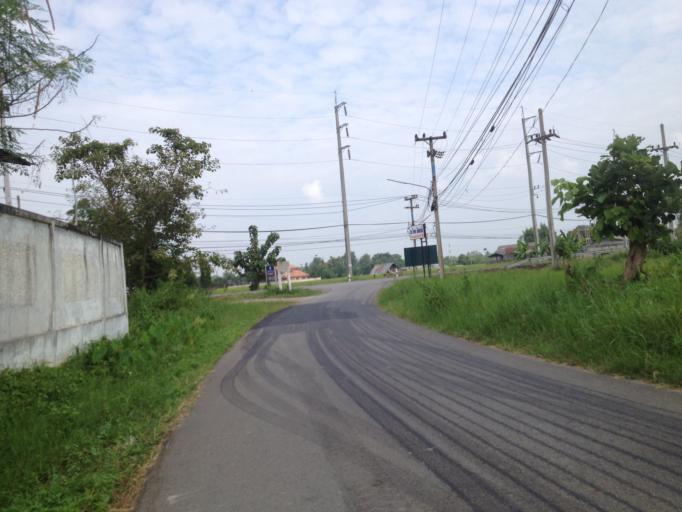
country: TH
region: Chiang Mai
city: Hang Dong
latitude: 18.6759
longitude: 98.9062
